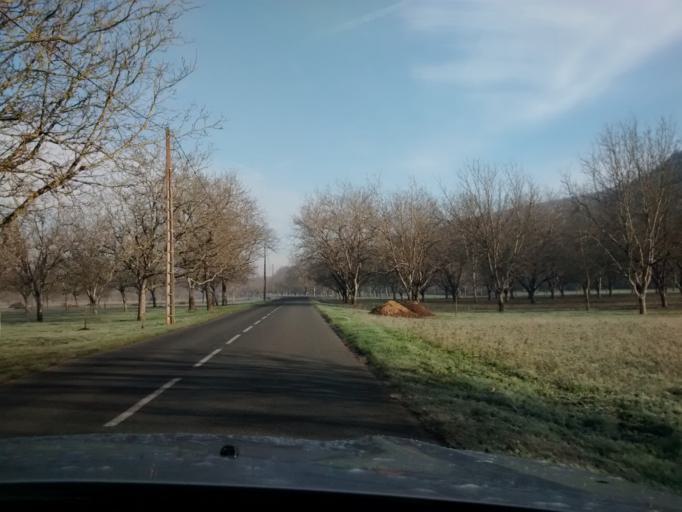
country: FR
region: Midi-Pyrenees
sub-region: Departement du Lot
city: Souillac
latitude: 44.8747
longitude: 1.4441
